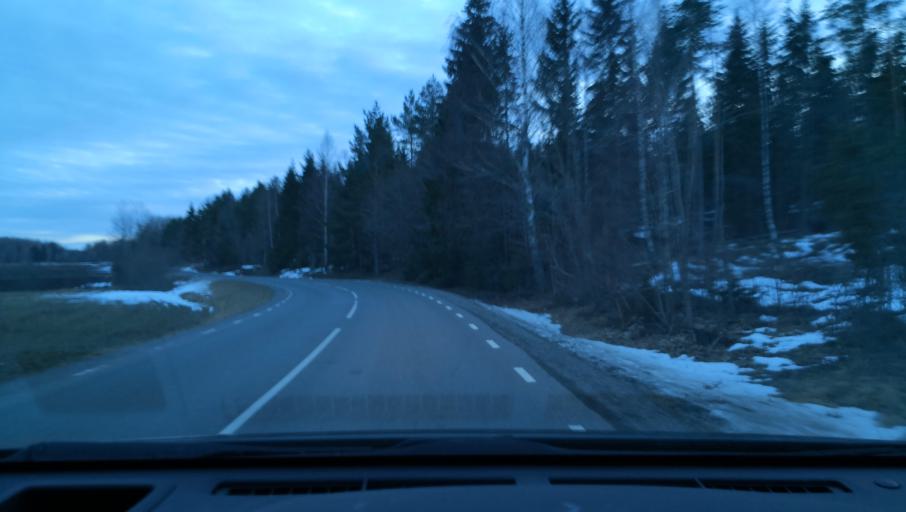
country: SE
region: Uppsala
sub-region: Osthammars Kommun
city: Bjorklinge
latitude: 60.1006
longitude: 17.5592
